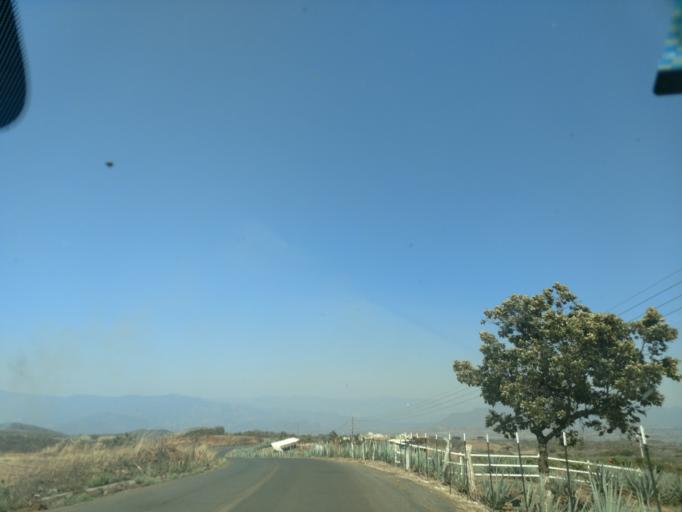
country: MX
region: Nayarit
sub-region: Tepic
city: La Corregidora
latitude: 21.4930
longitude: -104.6899
